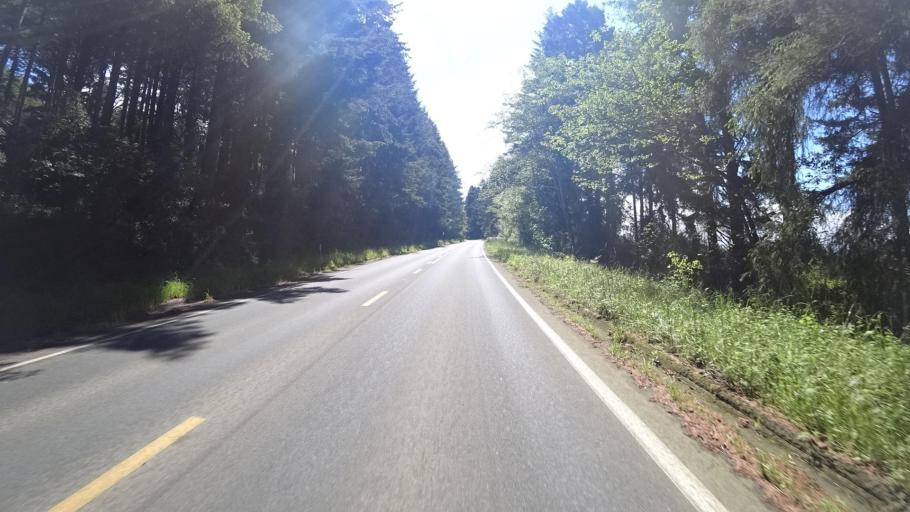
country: US
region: California
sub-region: Humboldt County
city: McKinleyville
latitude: 40.9553
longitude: -124.0854
